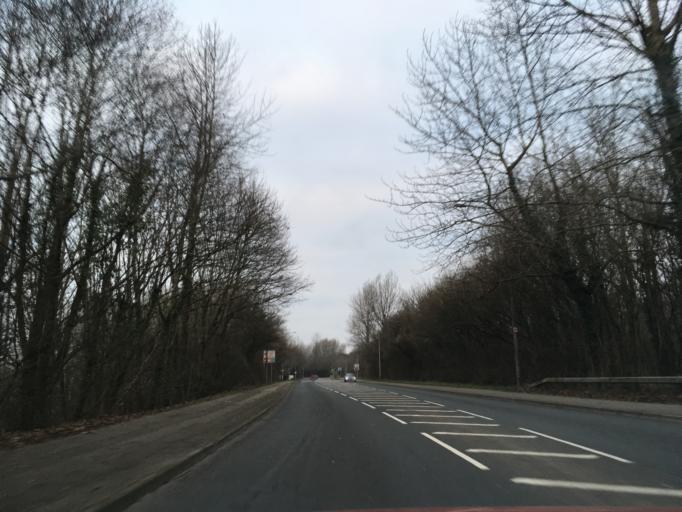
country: GB
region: Wales
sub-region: Newport
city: Newport
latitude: 51.5871
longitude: -3.0512
